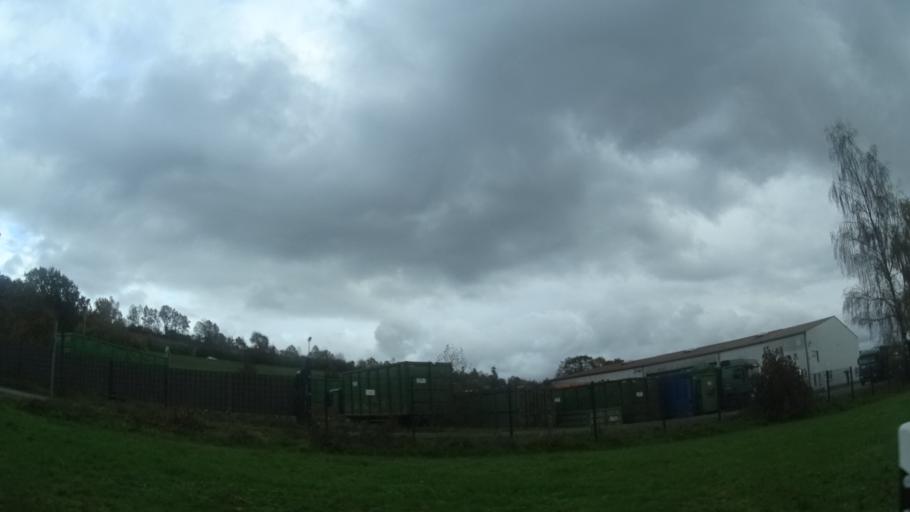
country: DE
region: Bavaria
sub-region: Regierungsbezirk Unterfranken
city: Oberelsbach
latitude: 50.3842
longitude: 10.1018
